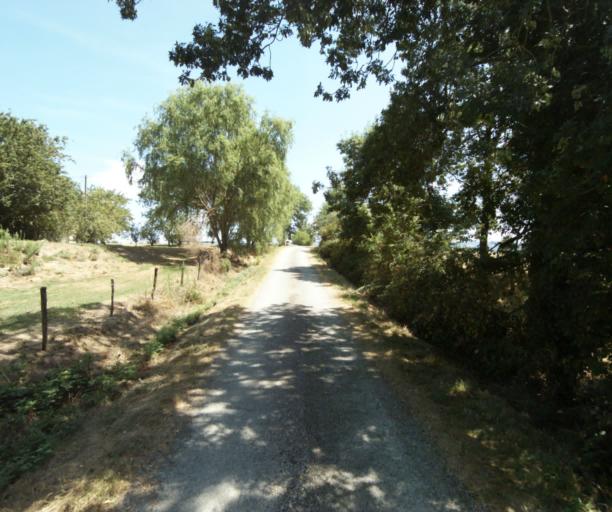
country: FR
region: Midi-Pyrenees
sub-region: Departement de la Haute-Garonne
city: Revel
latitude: 43.5032
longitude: 2.0233
